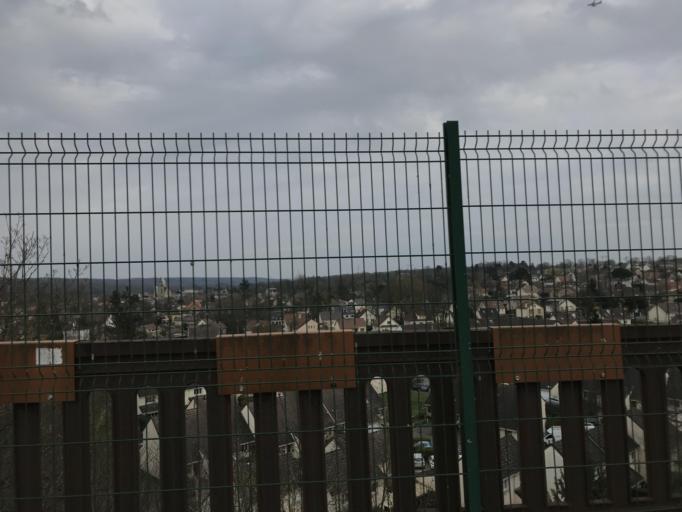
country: FR
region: Ile-de-France
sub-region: Departement de l'Essonne
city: Limours
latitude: 48.6478
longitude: 2.0666
